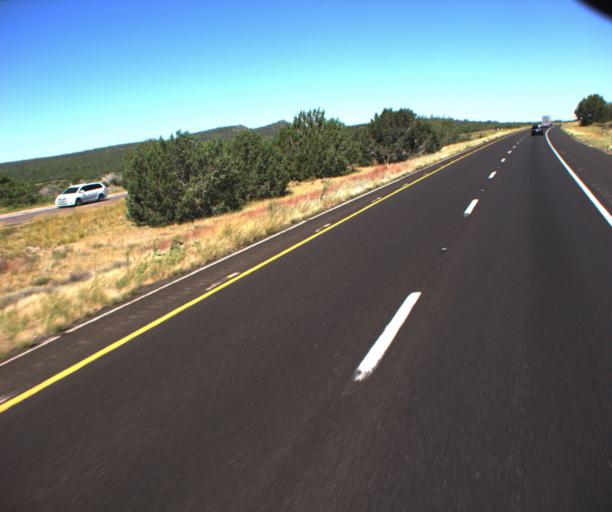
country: US
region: Arizona
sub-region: Yavapai County
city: Paulden
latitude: 35.2614
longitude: -112.7185
